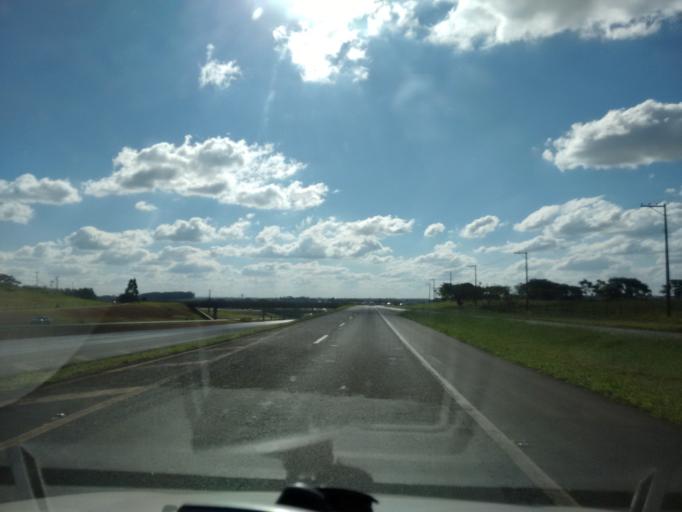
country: BR
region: Sao Paulo
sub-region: Araraquara
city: Araraquara
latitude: -21.8200
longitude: -48.1758
